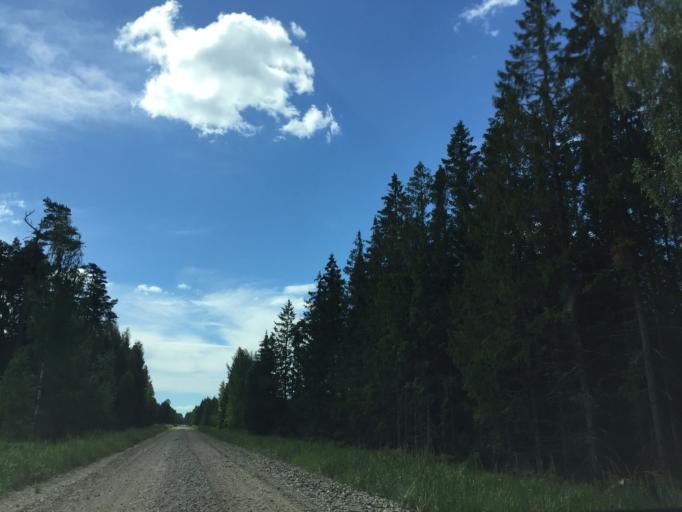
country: LV
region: Ventspils Rajons
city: Piltene
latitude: 57.2618
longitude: 21.8369
